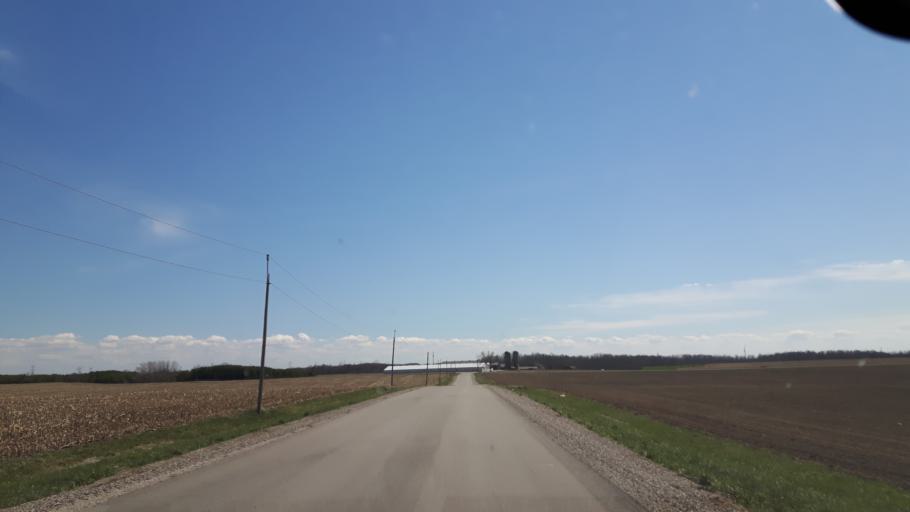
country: CA
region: Ontario
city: Bluewater
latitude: 43.5823
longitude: -81.6439
